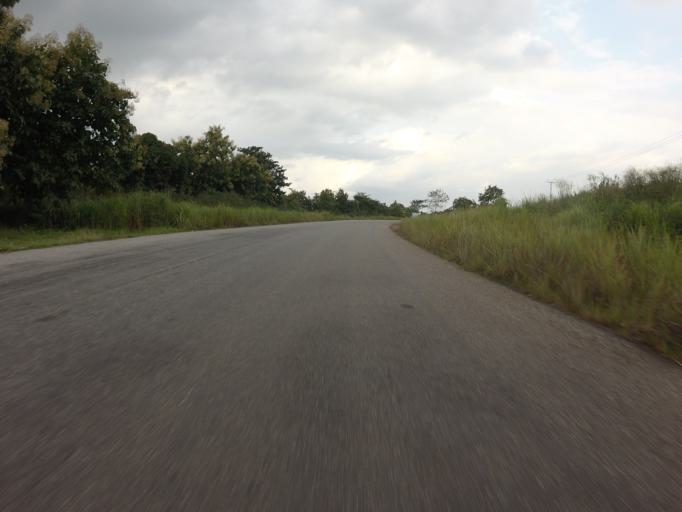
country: GH
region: Volta
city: Ho
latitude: 6.4267
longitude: 0.5161
